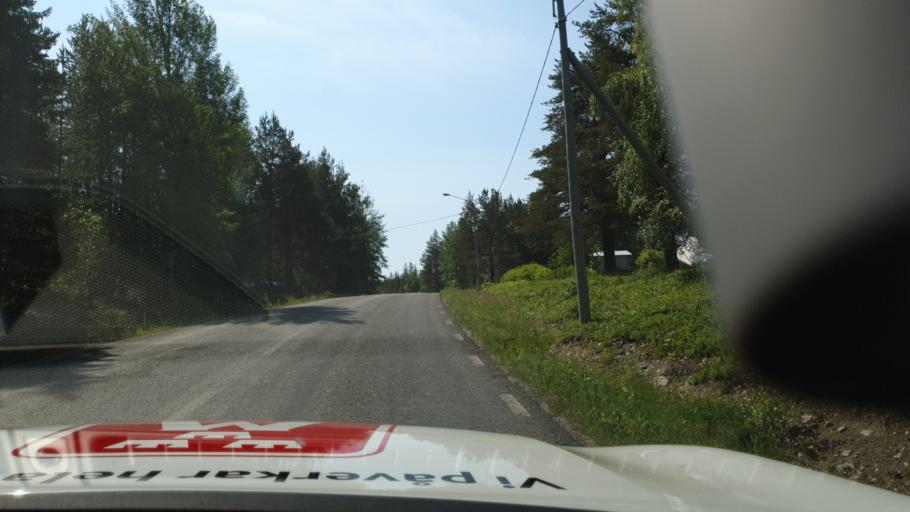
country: SE
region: Vaesterbotten
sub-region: Skelleftea Kommun
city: Langsele
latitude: 65.0049
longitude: 20.0907
